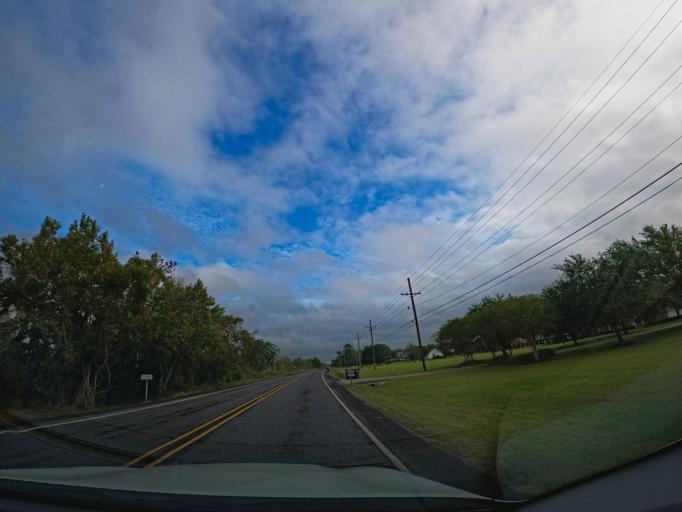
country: US
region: Louisiana
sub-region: Terrebonne Parish
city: Dulac
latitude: 29.4536
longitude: -90.7032
